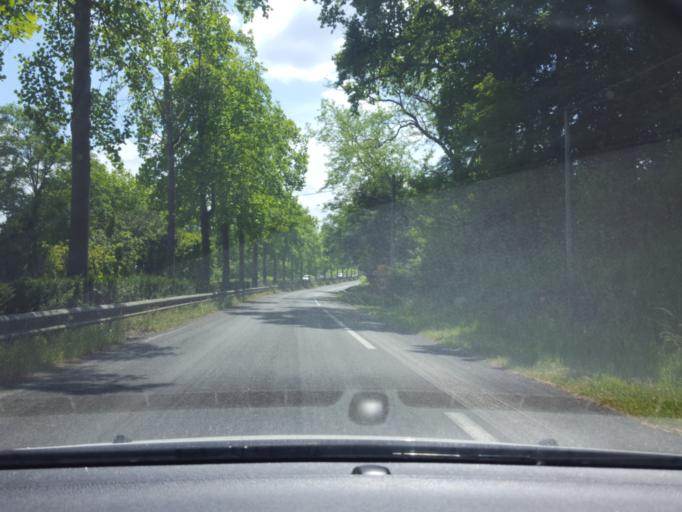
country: FR
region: Aquitaine
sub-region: Departement des Landes
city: Ondres
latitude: 43.5571
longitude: -1.4539
